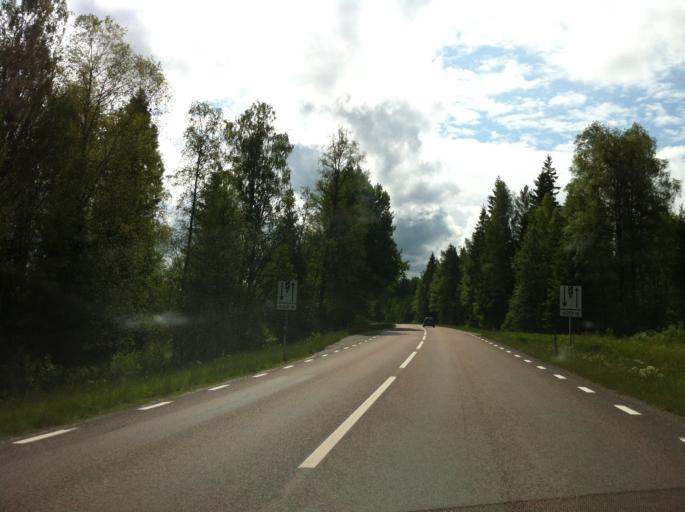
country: SE
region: Vaermland
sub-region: Karlstads Kommun
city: Edsvalla
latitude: 59.5472
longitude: 13.1963
